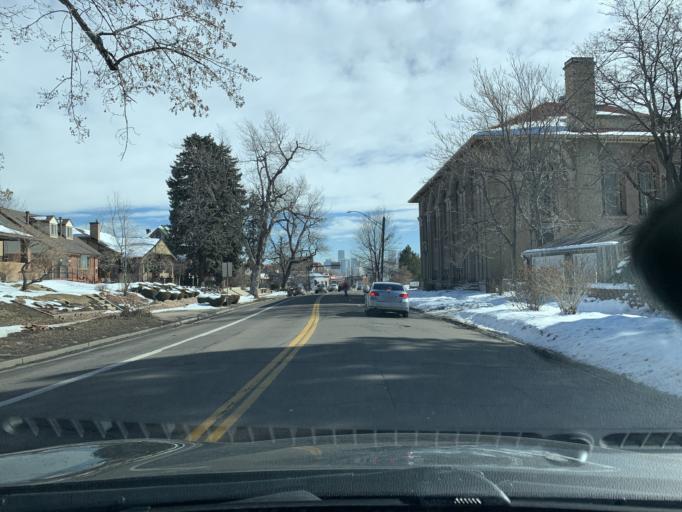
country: US
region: Colorado
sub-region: Jefferson County
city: Edgewater
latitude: 39.7615
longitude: -105.0280
